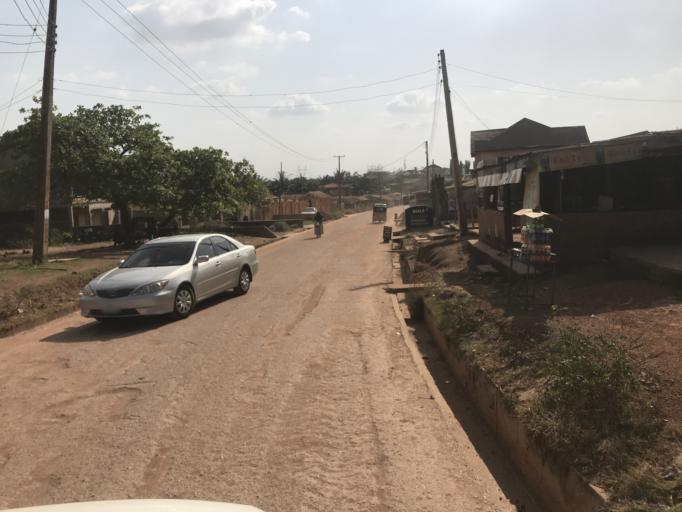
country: NG
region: Osun
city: Osogbo
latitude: 7.8062
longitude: 4.5574
